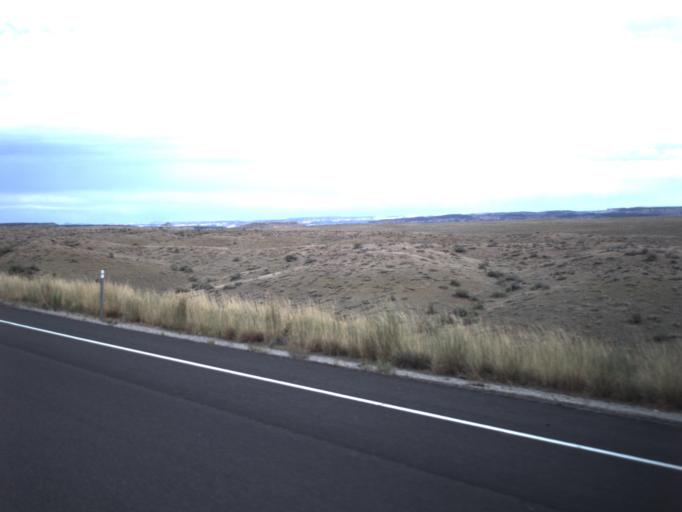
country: US
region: Colorado
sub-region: Mesa County
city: Loma
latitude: 39.0405
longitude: -109.2790
